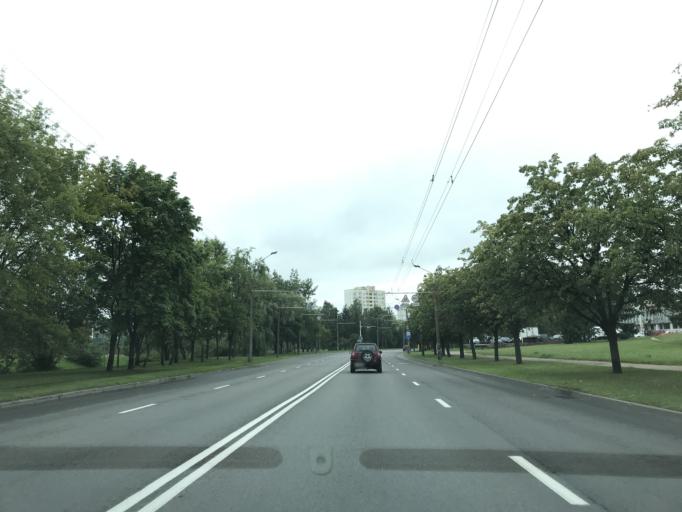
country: BY
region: Minsk
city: Borovlyany
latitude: 53.9403
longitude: 27.6433
